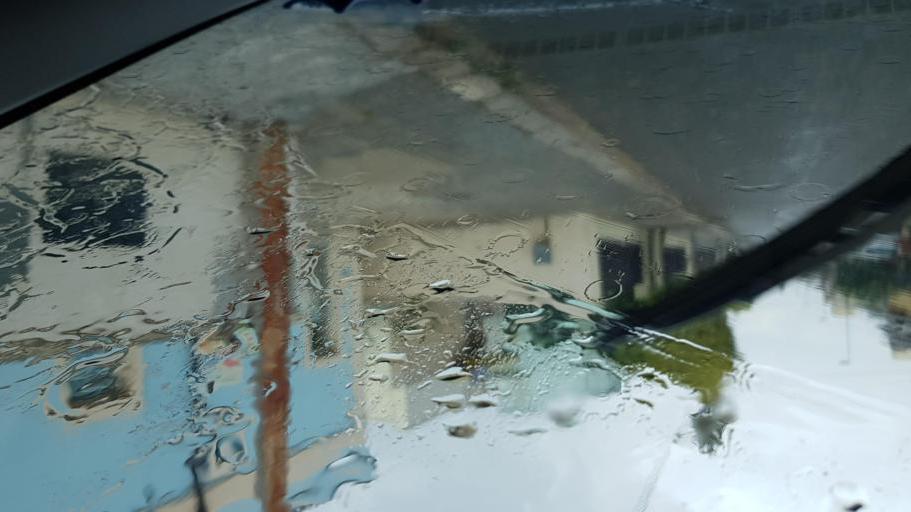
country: IT
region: Apulia
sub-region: Provincia di Lecce
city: Taurisano
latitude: 39.9557
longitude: 18.2210
